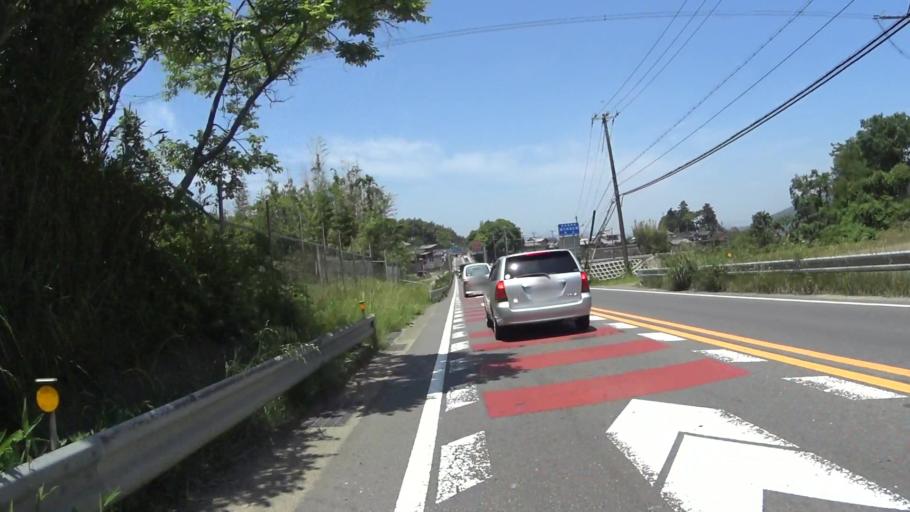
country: JP
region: Kyoto
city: Kameoka
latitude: 34.9940
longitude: 135.6212
